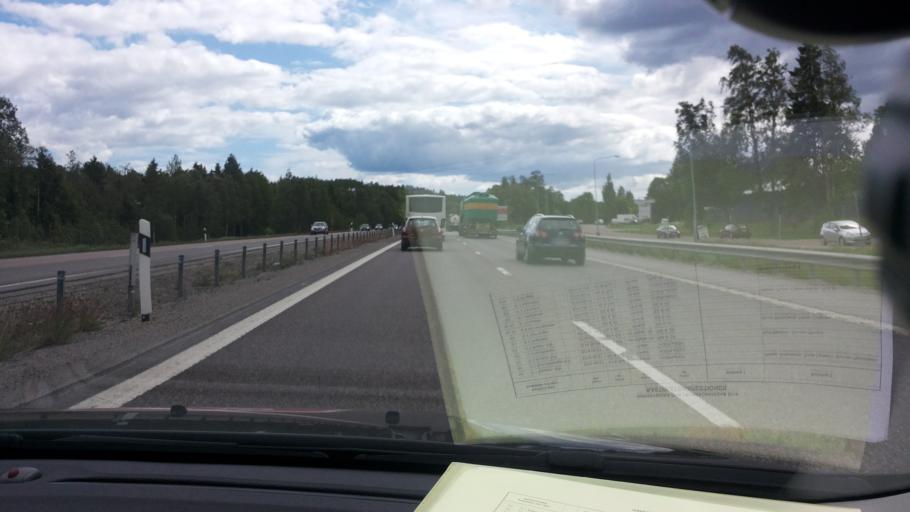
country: SE
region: Vaesternorrland
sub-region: Sundsvalls Kommun
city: Sundsbruk
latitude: 62.4312
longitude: 17.3444
